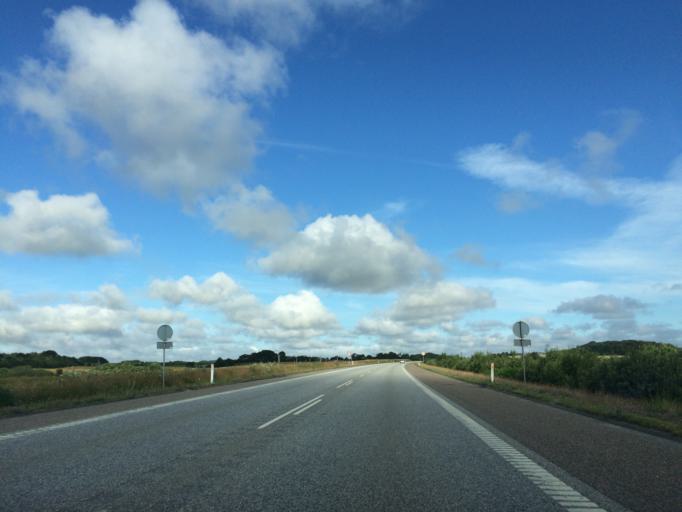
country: DK
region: Central Jutland
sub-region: Silkeborg Kommune
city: Kjellerup
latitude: 56.3652
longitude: 9.4829
